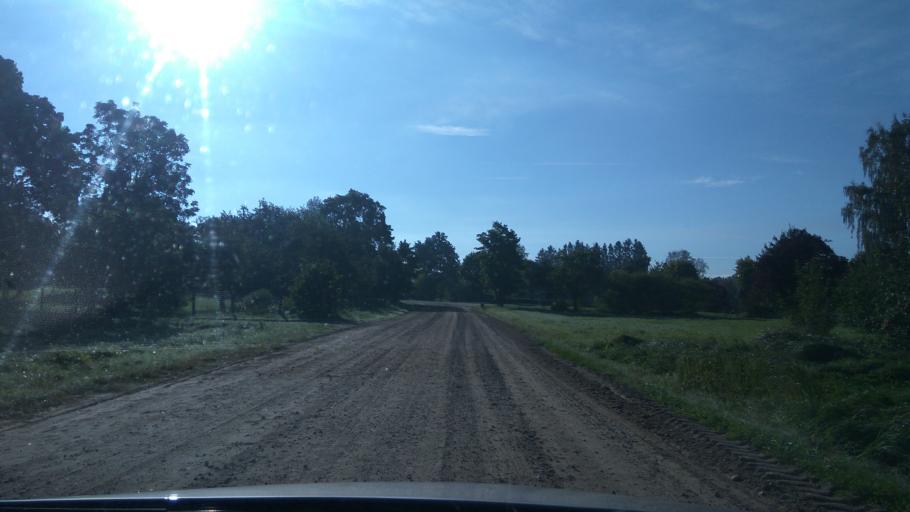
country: LV
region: Kuldigas Rajons
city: Kuldiga
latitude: 56.9727
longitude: 21.9946
